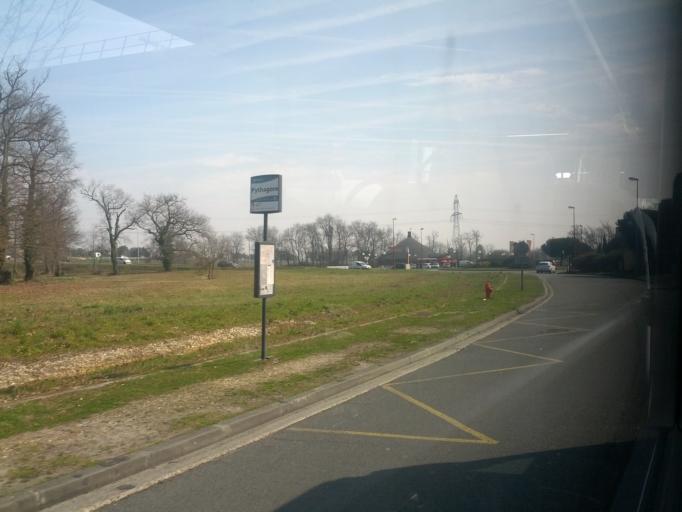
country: FR
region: Aquitaine
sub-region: Departement de la Gironde
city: Le Haillan
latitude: 44.8316
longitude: -0.6810
